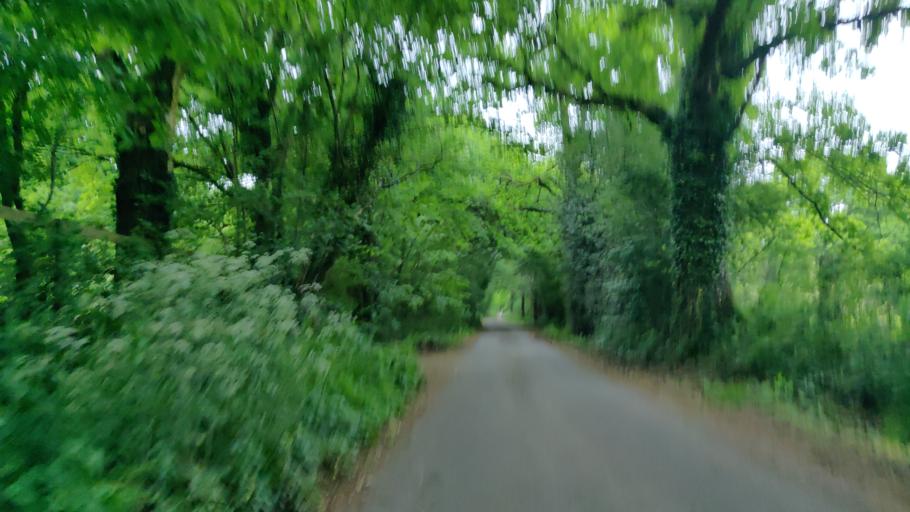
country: GB
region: England
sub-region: West Sussex
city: Southwater
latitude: 51.0171
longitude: -0.3322
